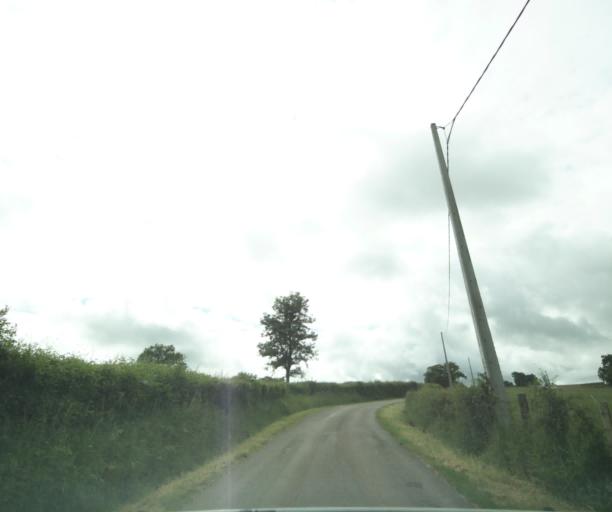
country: FR
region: Bourgogne
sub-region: Departement de Saone-et-Loire
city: Charolles
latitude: 46.4213
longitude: 4.3062
